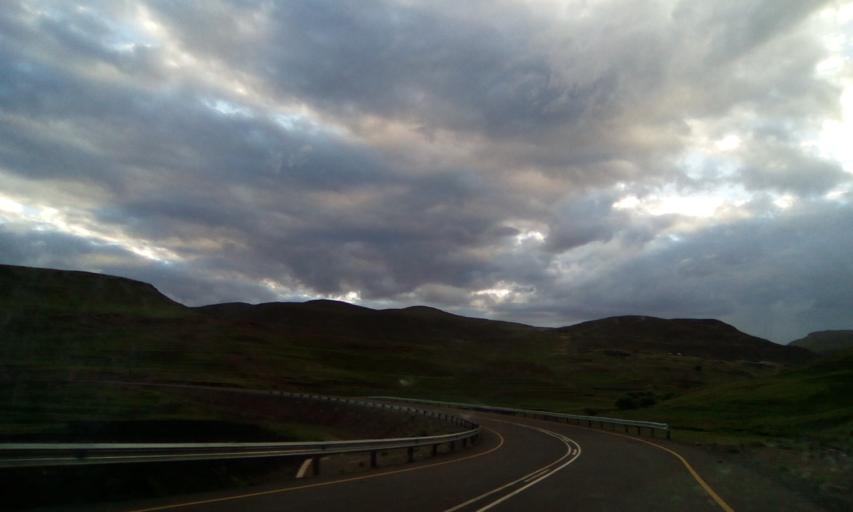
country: LS
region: Maseru
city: Nako
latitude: -29.8049
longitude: 28.0286
